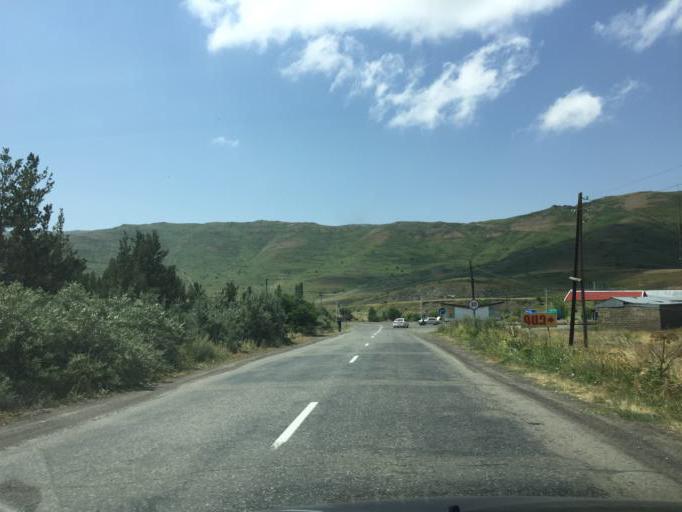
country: AM
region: Geghark'unik'i Marz
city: Tsovagyugh
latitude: 40.6108
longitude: 44.9560
